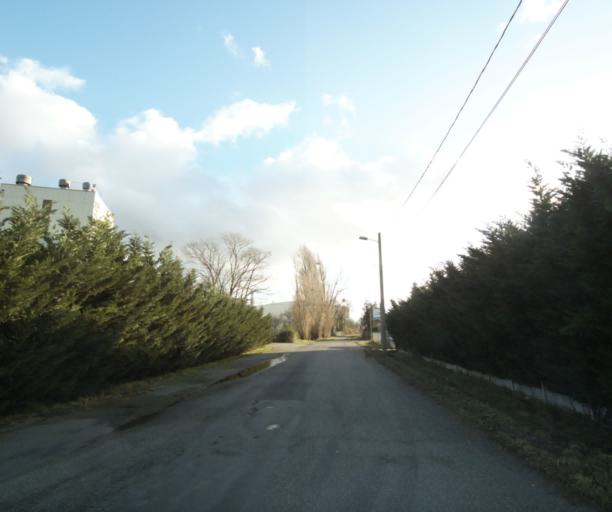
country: FR
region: Pays de la Loire
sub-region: Departement de la Sarthe
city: Allonnes
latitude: 47.9843
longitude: 0.1668
